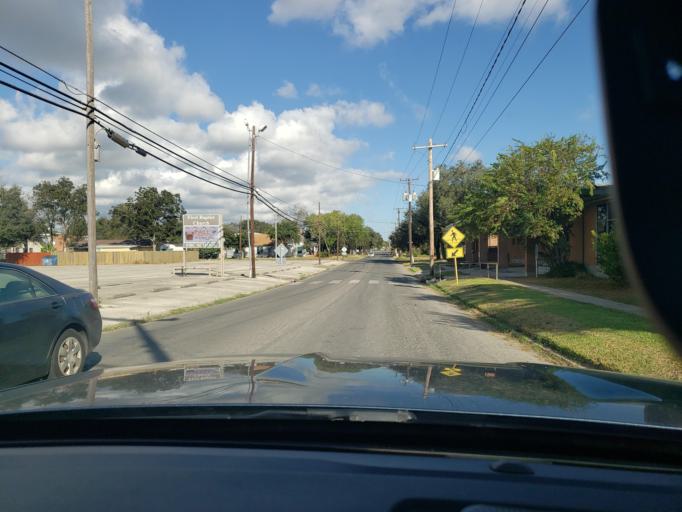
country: US
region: Texas
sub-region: Bee County
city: Beeville
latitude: 28.4065
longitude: -97.7507
